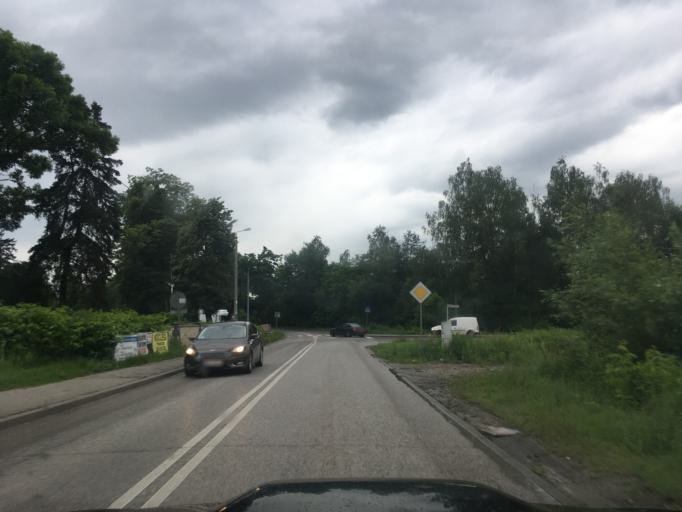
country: PL
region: Masovian Voivodeship
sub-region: Powiat piaseczynski
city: Zalesie Gorne
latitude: 52.0408
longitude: 21.0029
